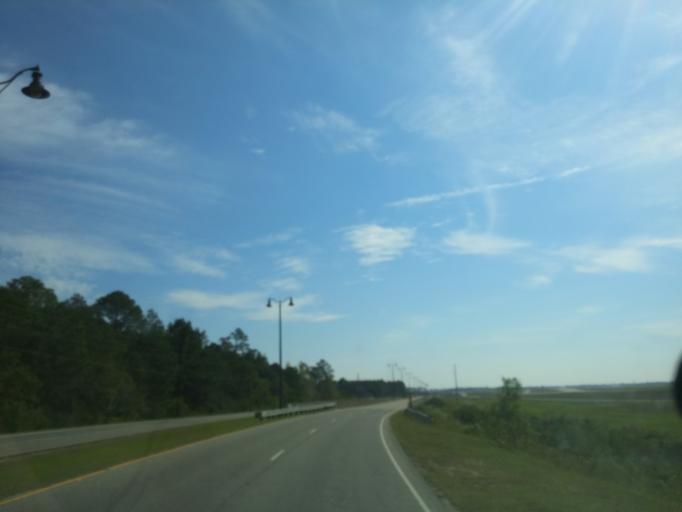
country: US
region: Mississippi
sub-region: Harrison County
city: West Gulfport
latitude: 30.4191
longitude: -89.0836
